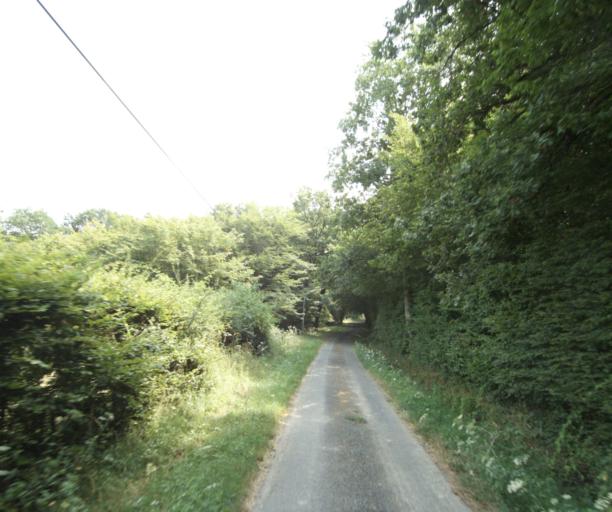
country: FR
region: Bourgogne
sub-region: Departement de Saone-et-Loire
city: Gueugnon
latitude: 46.6047
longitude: 4.0219
